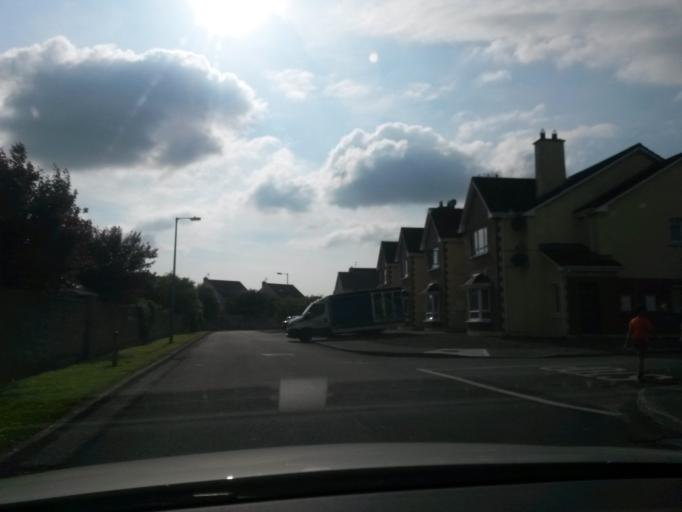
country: IE
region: Munster
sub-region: An Clar
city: Ennis
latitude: 52.8378
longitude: -8.9620
